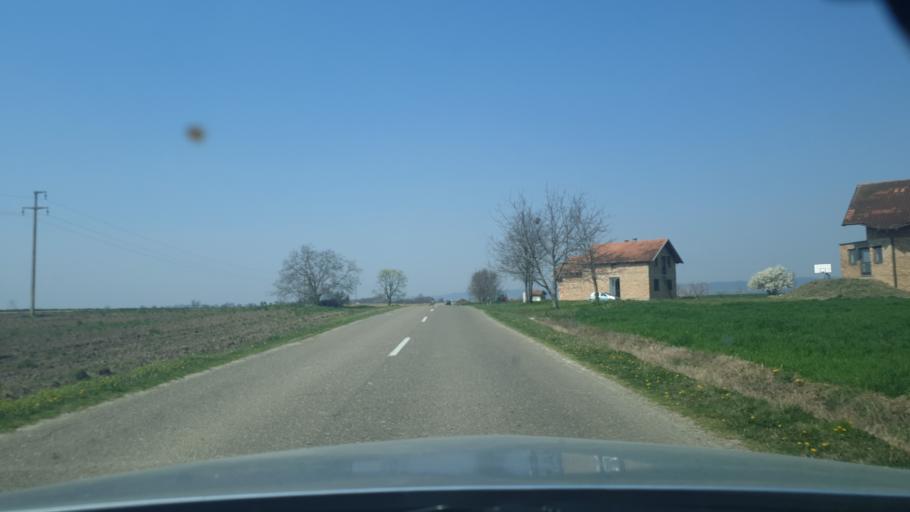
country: RS
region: Autonomna Pokrajina Vojvodina
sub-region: Sremski Okrug
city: Ruma
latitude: 45.0130
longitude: 19.7808
